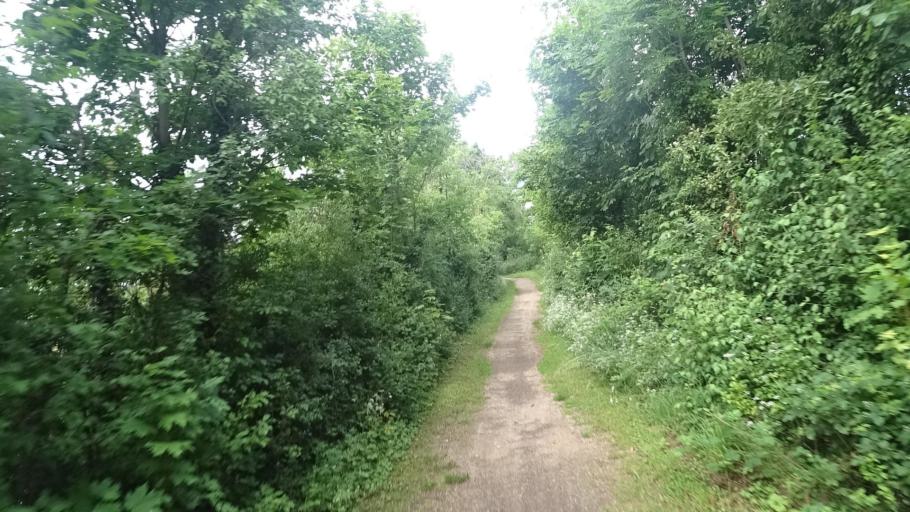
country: DE
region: Rheinland-Pfalz
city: Bad Neuenahr-Ahrweiler
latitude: 50.5700
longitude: 7.0945
